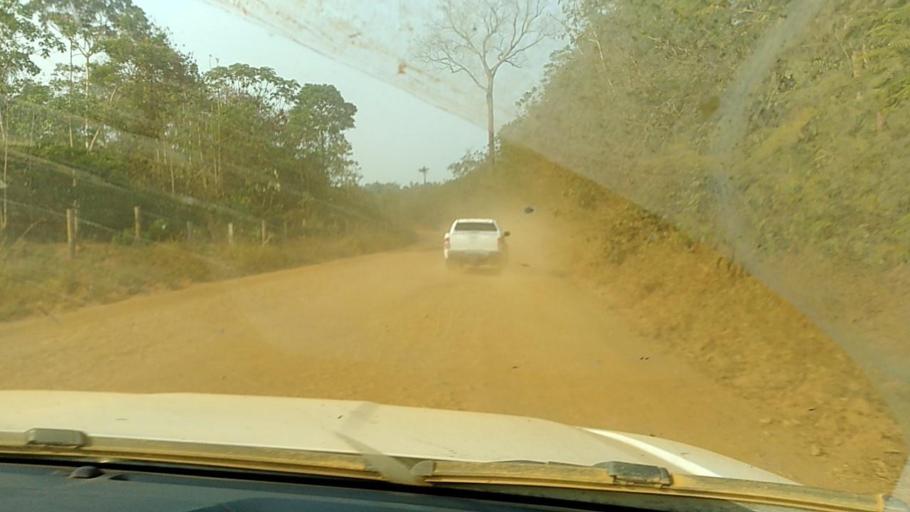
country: BR
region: Rondonia
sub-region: Porto Velho
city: Porto Velho
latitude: -8.7451
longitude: -63.9643
